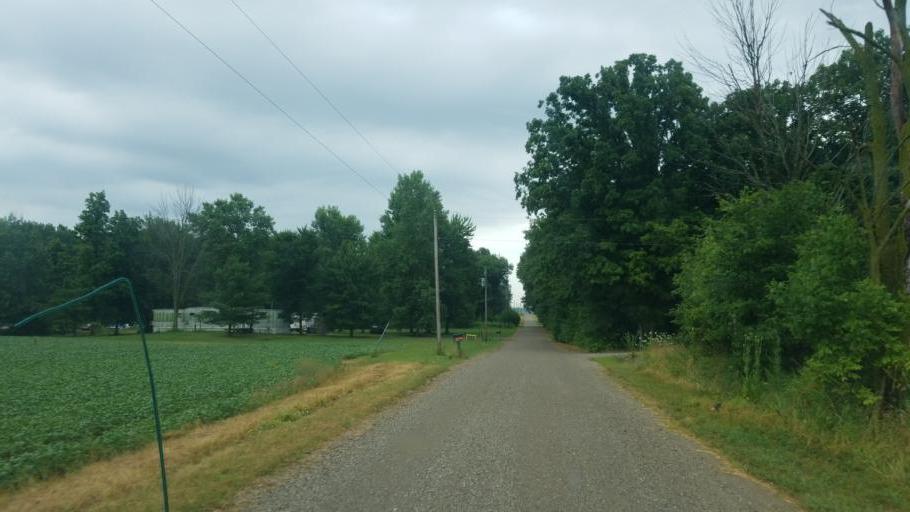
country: US
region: Indiana
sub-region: Steuben County
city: Hamilton
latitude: 41.4810
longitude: -84.9106
